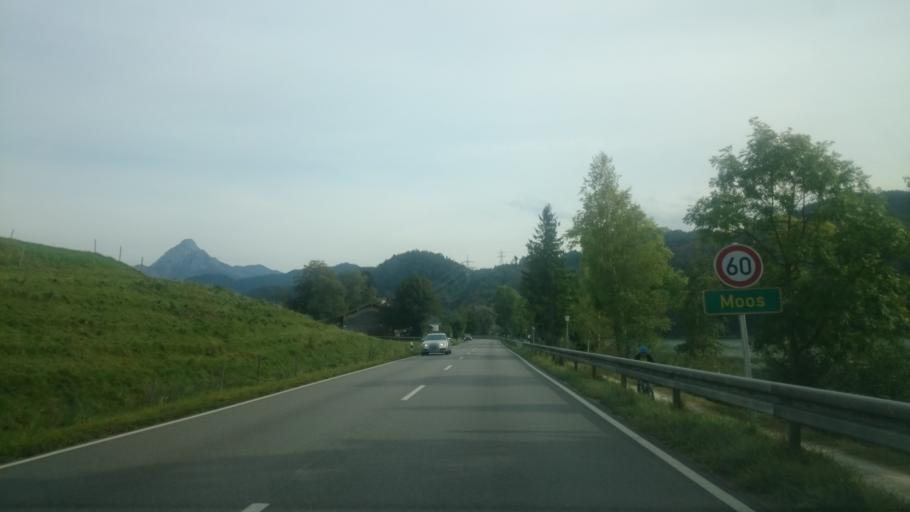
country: AT
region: Tyrol
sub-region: Politischer Bezirk Reutte
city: Vils
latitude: 47.5742
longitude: 10.6450
